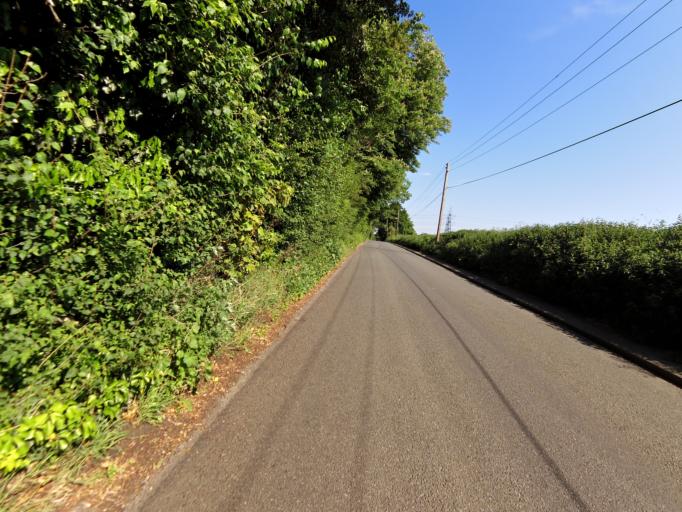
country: GB
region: England
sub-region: Suffolk
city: Bramford
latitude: 52.0808
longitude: 1.1052
